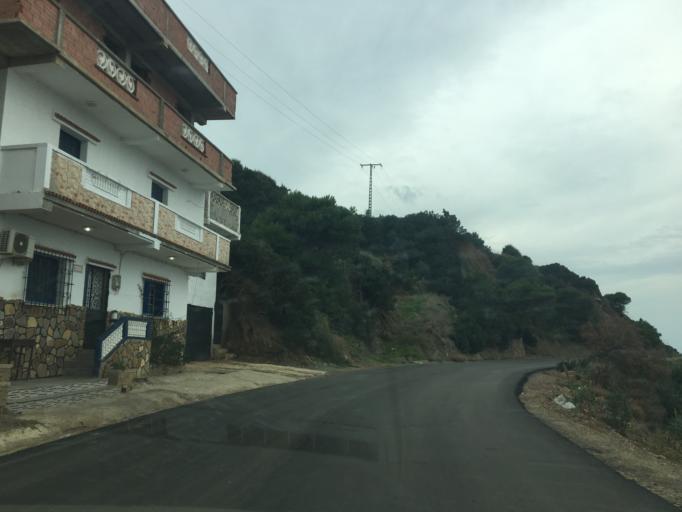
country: DZ
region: Tipaza
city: Tipasa
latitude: 36.6404
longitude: 2.3419
